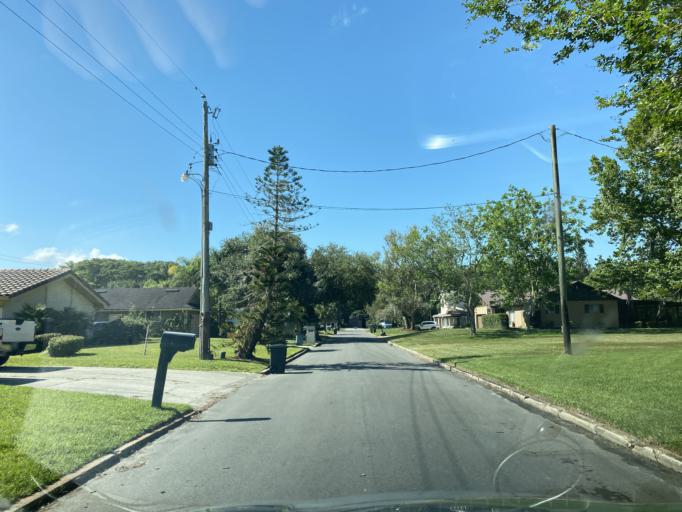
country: US
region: Florida
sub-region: Volusia County
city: DeBary
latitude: 28.8386
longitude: -81.3332
